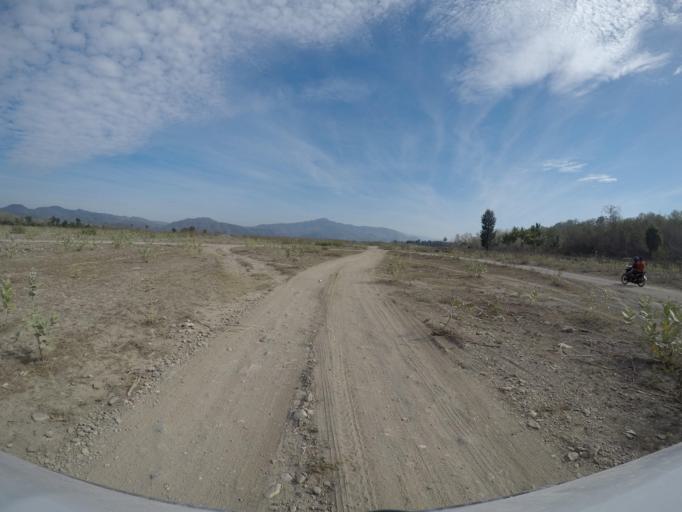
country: TL
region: Bobonaro
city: Maliana
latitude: -8.8919
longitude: 125.2081
